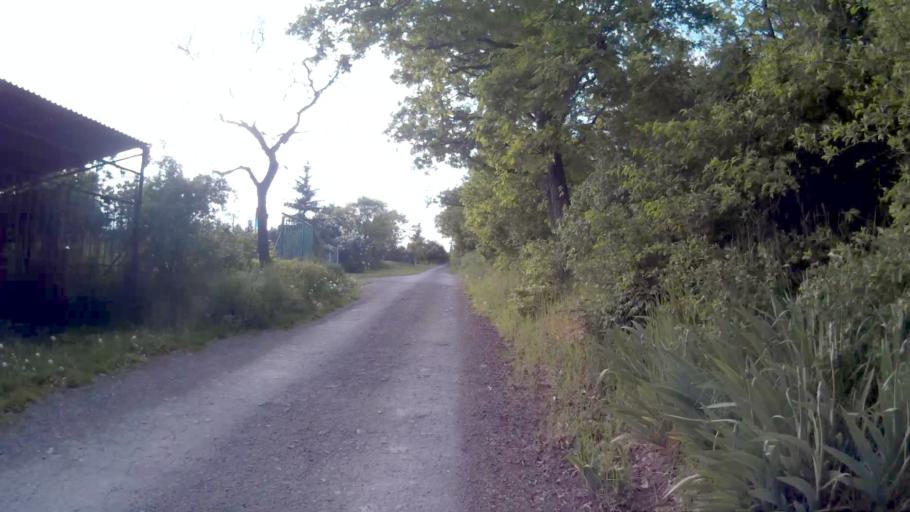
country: CZ
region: South Moravian
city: Troubsko
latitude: 49.1844
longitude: 16.5253
